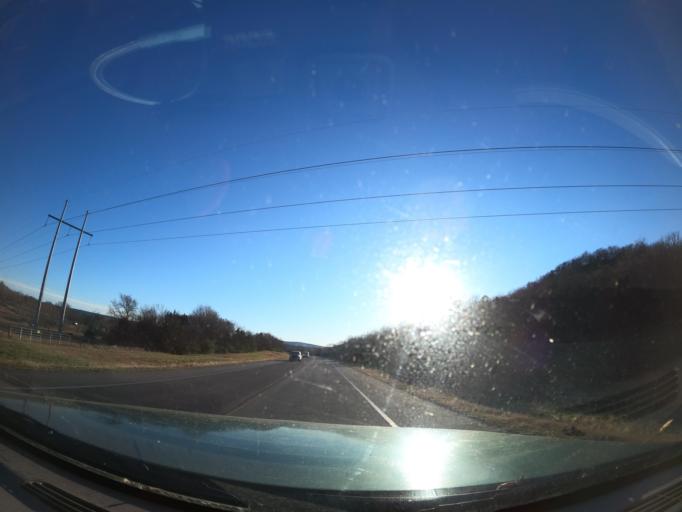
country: US
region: Oklahoma
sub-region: Pittsburg County
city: Hartshorne
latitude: 34.8581
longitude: -95.5318
